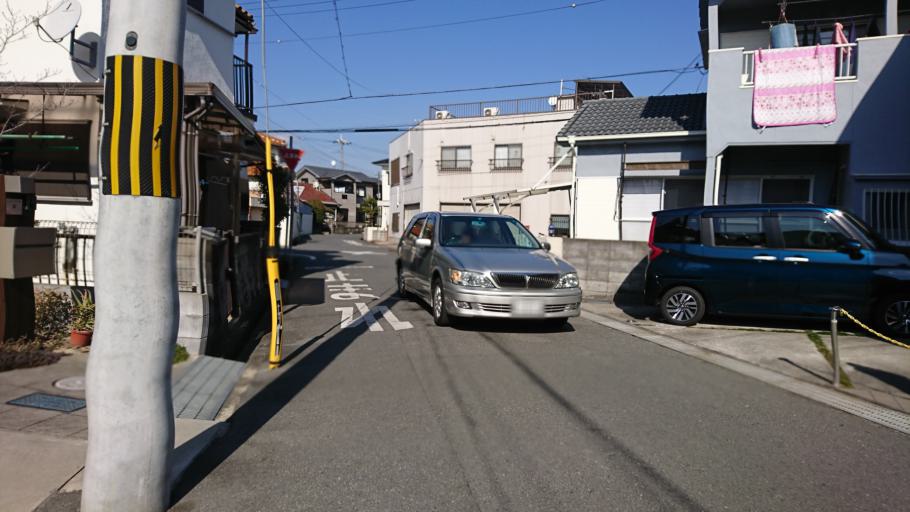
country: JP
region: Hyogo
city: Kakogawacho-honmachi
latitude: 34.7395
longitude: 134.8681
